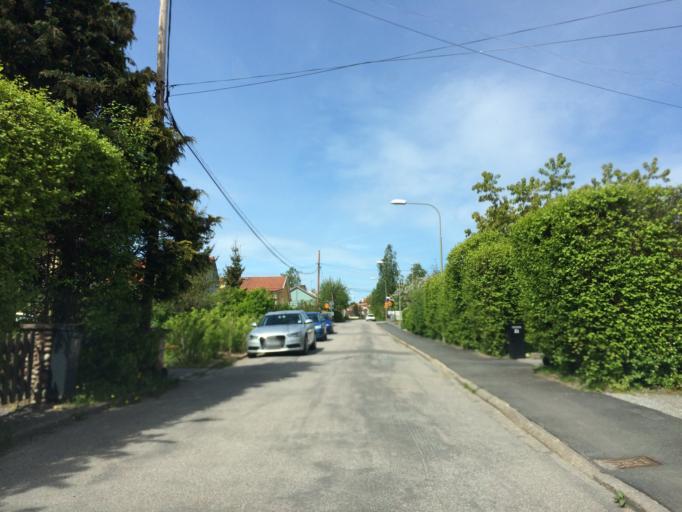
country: SE
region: Stockholm
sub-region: Huddinge Kommun
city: Huddinge
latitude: 59.2850
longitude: 17.9952
